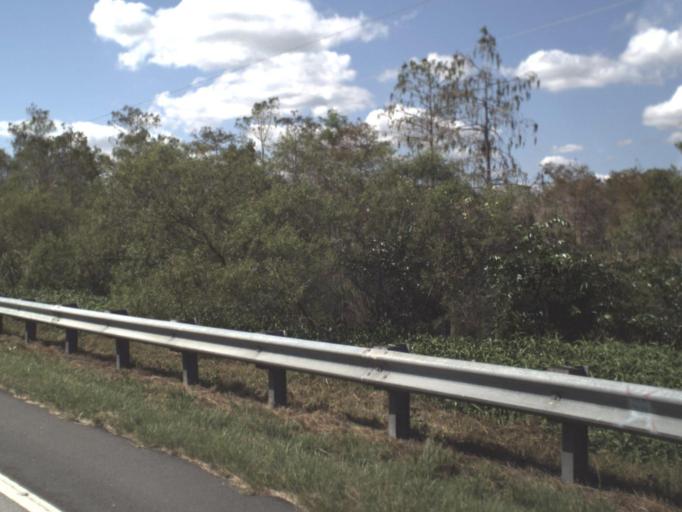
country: US
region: Florida
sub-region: Miami-Dade County
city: Kendall West
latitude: 25.8605
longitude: -81.0687
